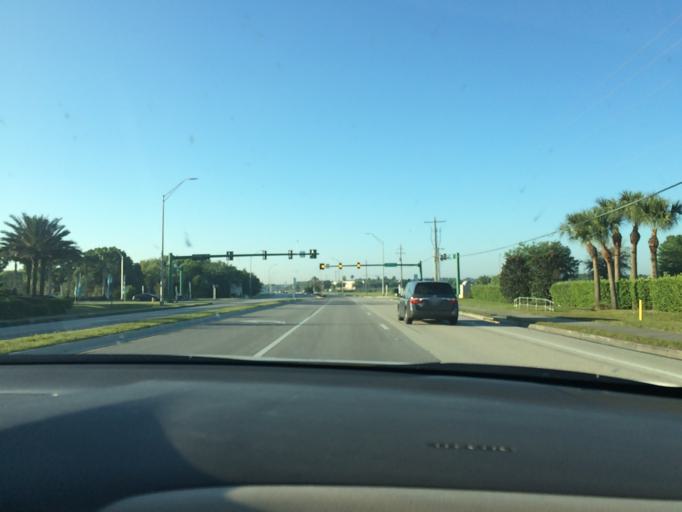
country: US
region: Florida
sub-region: Sarasota County
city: The Meadows
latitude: 27.4499
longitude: -82.4326
